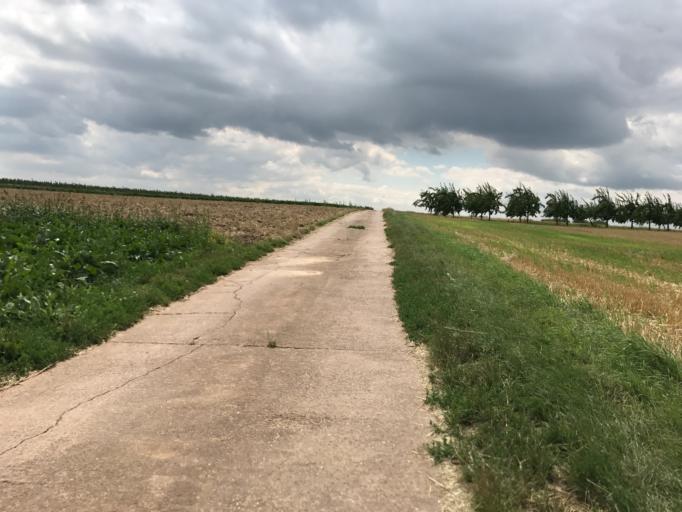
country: DE
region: Rheinland-Pfalz
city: Essenheim
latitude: 49.9539
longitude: 8.1510
